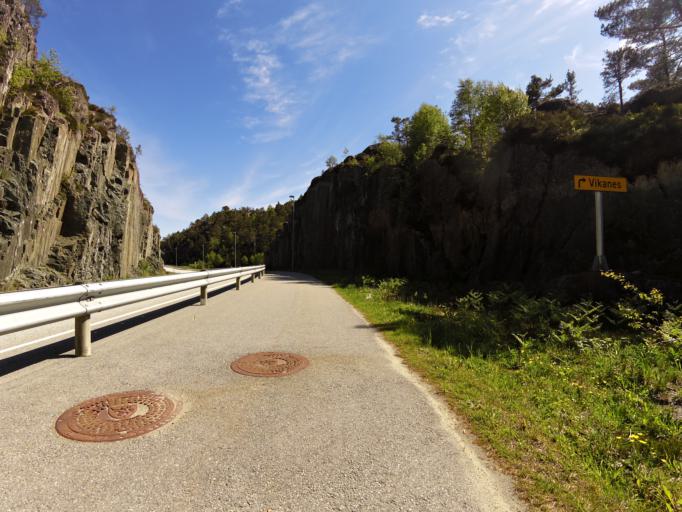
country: NO
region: Hordaland
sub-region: Stord
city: Sagvag
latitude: 59.7842
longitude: 5.3745
